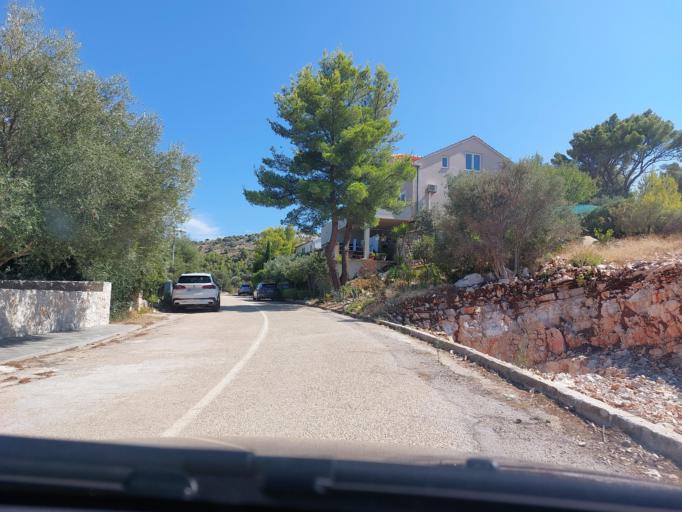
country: HR
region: Dubrovacko-Neretvanska
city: Smokvica
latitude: 42.7323
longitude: 16.8848
